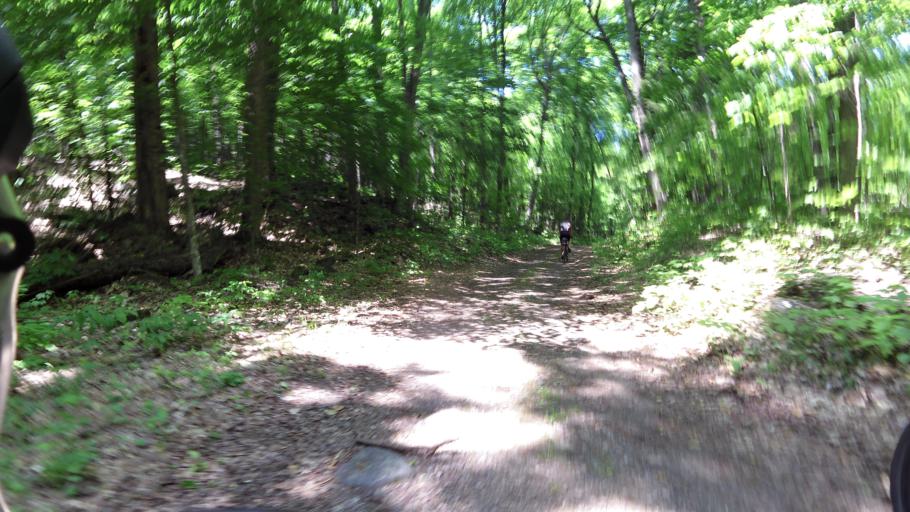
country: CA
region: Quebec
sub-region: Outaouais
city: Wakefield
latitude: 45.5796
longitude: -75.9509
